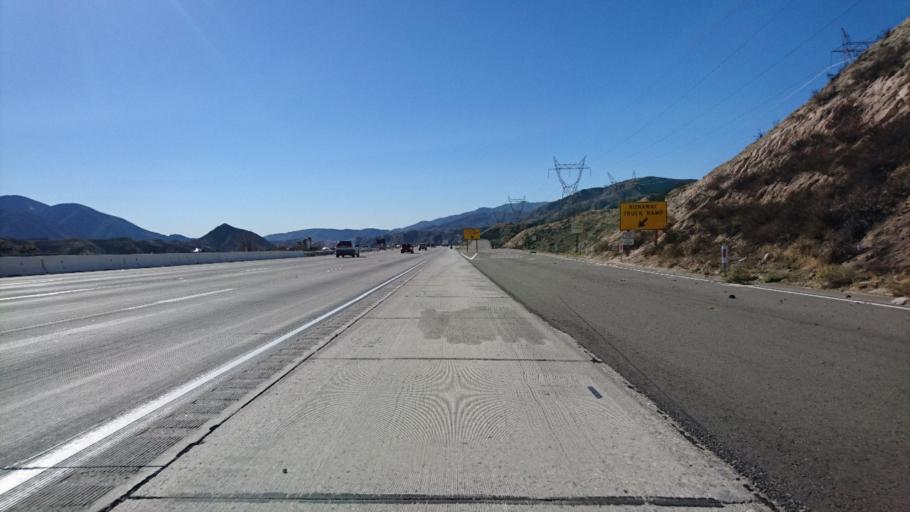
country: US
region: California
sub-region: San Bernardino County
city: Oak Hills
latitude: 34.3355
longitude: -117.4826
